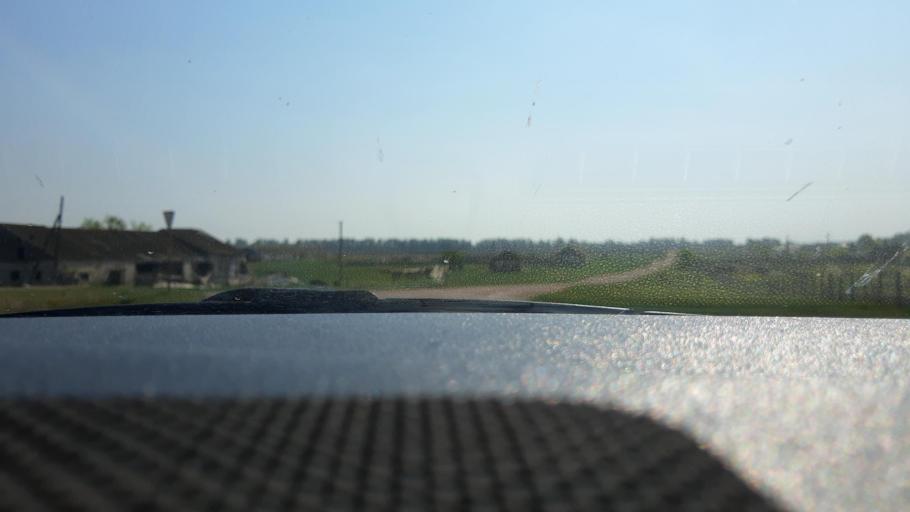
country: RU
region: Bashkortostan
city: Chishmy
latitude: 54.4468
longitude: 55.3185
